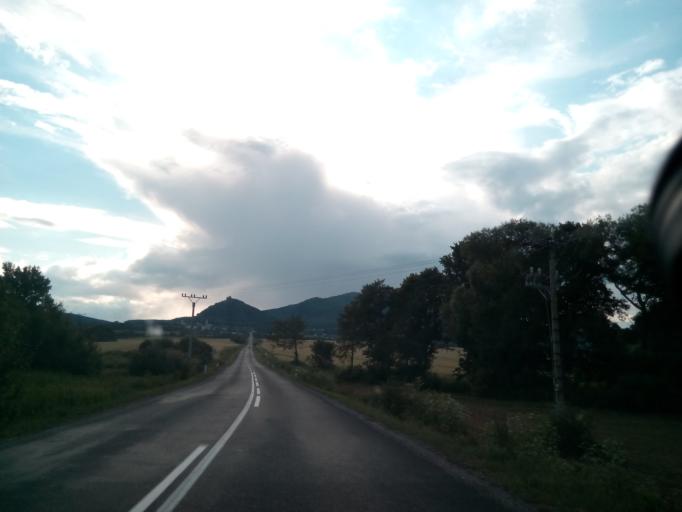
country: SK
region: Kosicky
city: Secovce
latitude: 48.6343
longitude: 21.5082
